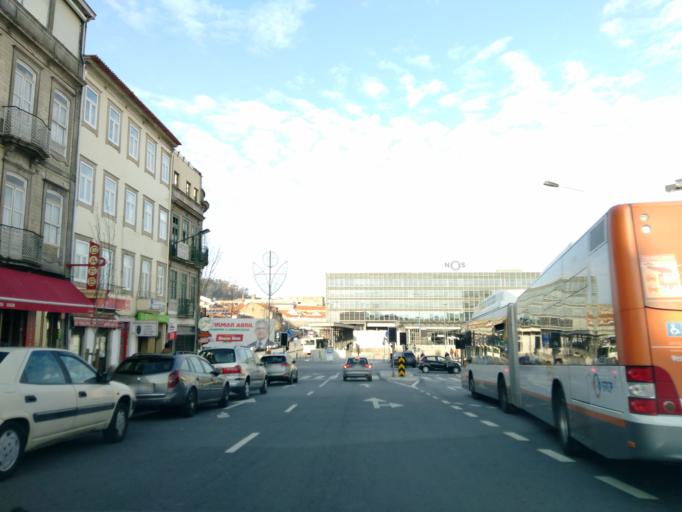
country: PT
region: Porto
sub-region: Vila Nova de Gaia
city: Oliveira do Douro
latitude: 41.1483
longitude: -8.5861
